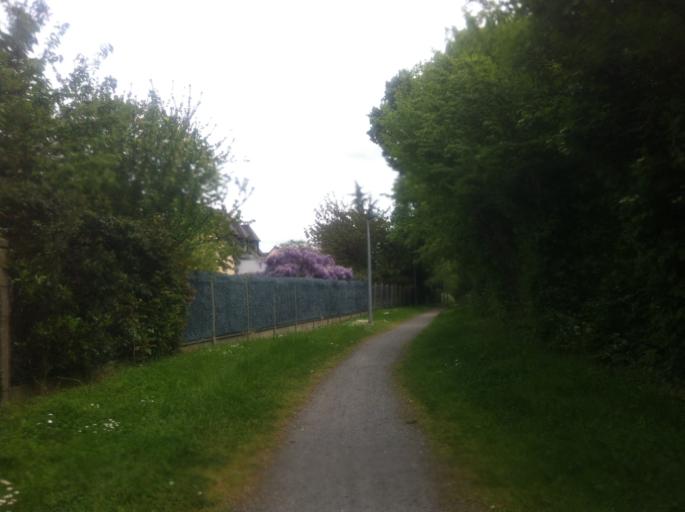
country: FR
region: Brittany
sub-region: Departement d'Ille-et-Vilaine
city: Chartres-de-Bretagne
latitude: 48.0364
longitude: -1.7110
